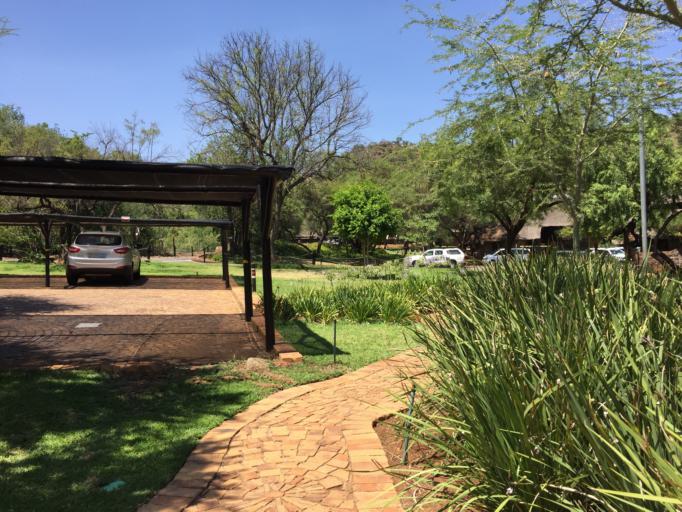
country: ZA
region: North-West
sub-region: Bojanala Platinum District Municipality
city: Mogwase
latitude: -25.3451
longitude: 27.0563
